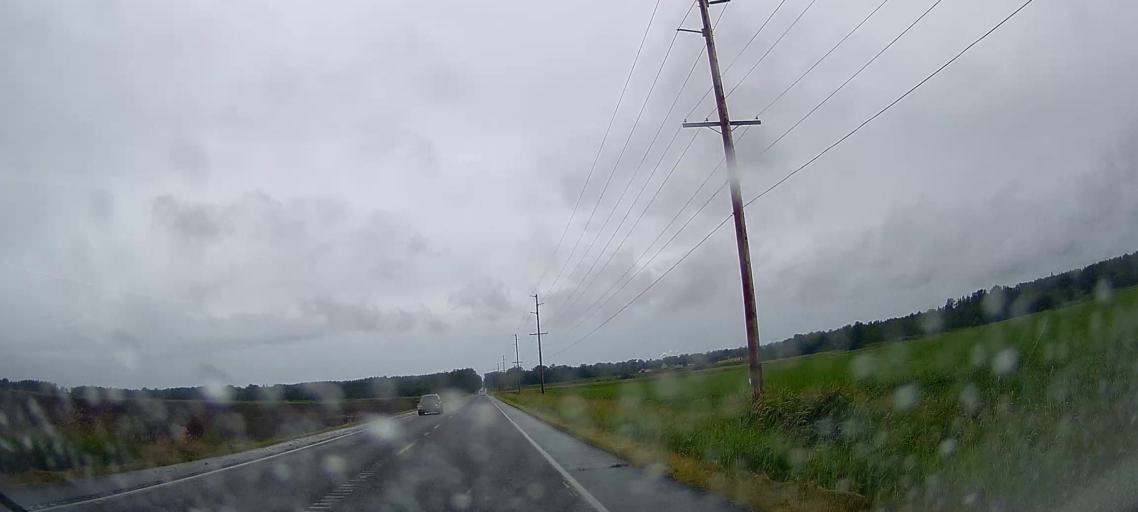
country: US
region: Washington
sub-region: Whatcom County
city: Ferndale
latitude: 48.8198
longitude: -122.6279
